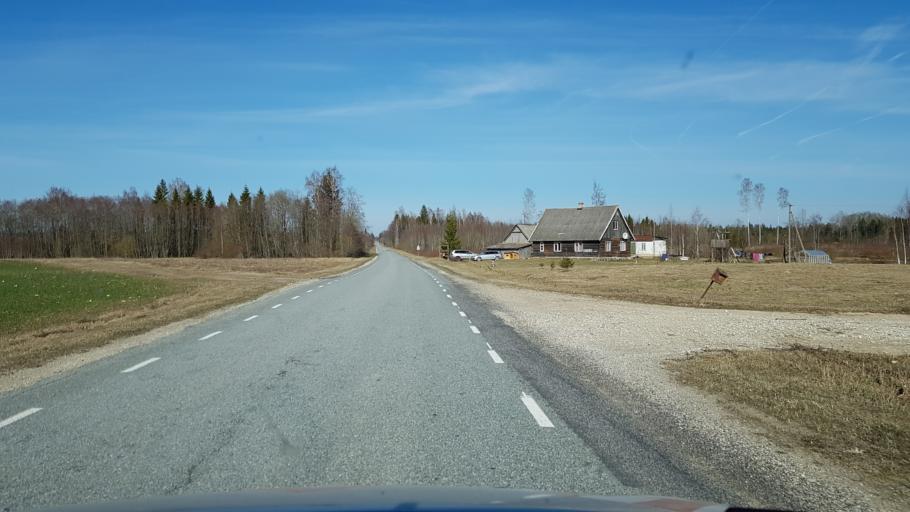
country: EE
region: Laeaene-Virumaa
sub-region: Rakke vald
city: Rakke
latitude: 59.0083
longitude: 26.3307
